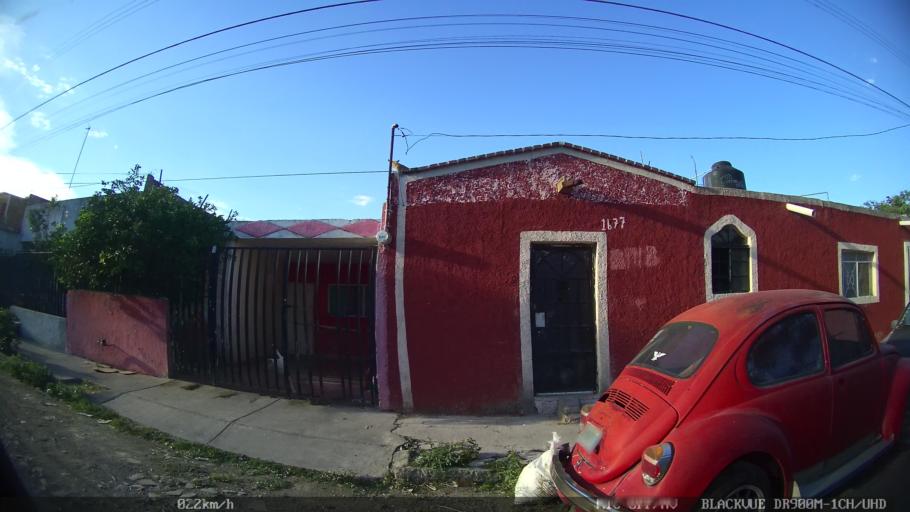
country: MX
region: Jalisco
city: Tlaquepaque
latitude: 20.7055
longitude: -103.2988
